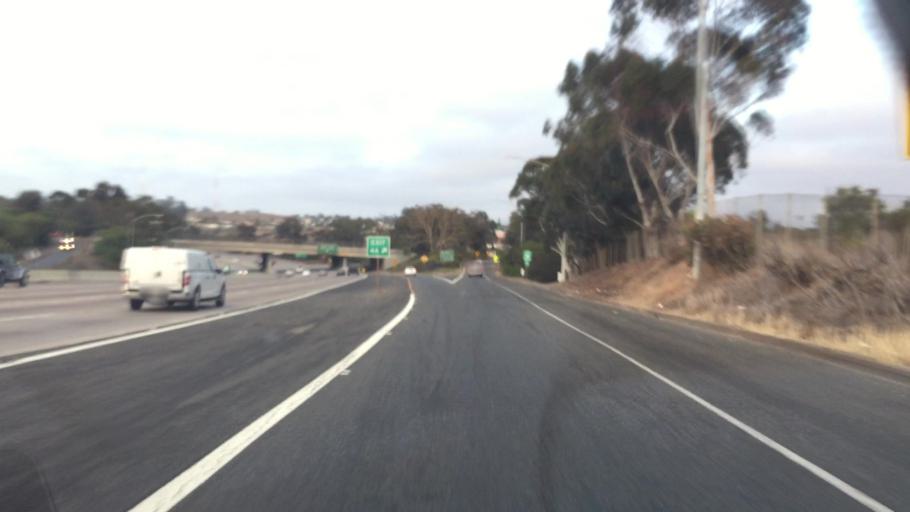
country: US
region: California
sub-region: San Diego County
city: National City
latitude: 32.7176
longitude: -117.0880
